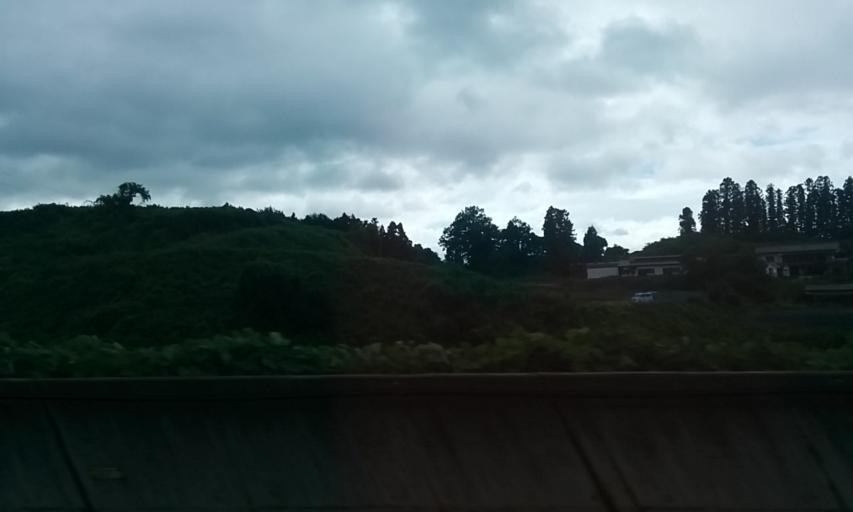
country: JP
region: Fukushima
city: Nihommatsu
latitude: 37.5414
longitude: 140.4459
